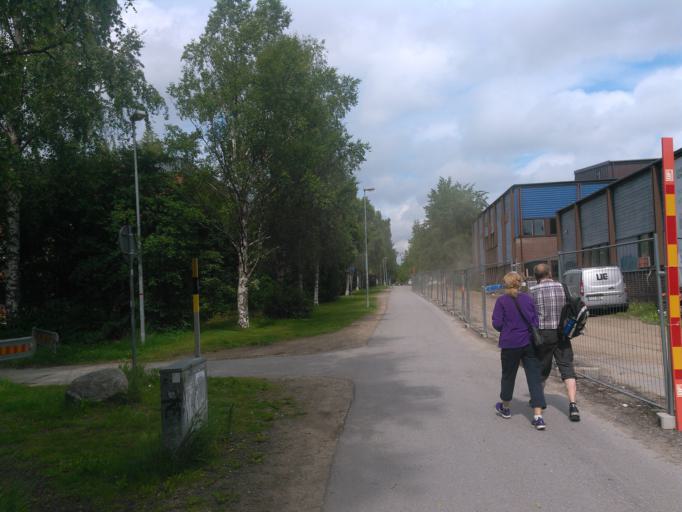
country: SE
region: Vaesterbotten
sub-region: Umea Kommun
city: Umea
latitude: 63.8108
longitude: 20.3133
